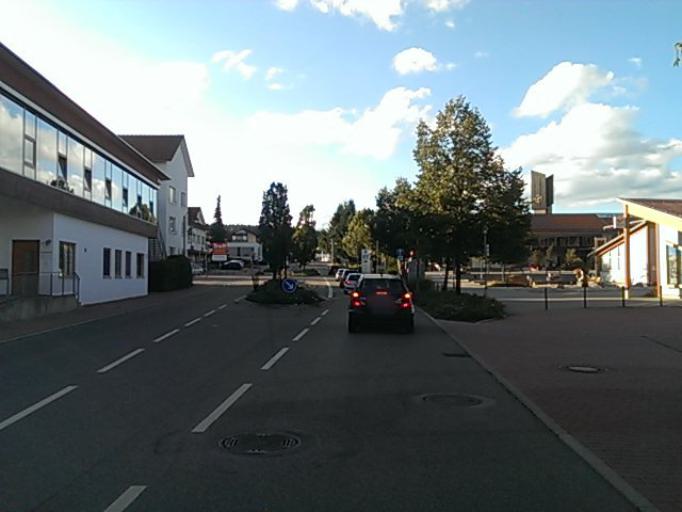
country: DE
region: Baden-Wuerttemberg
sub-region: Karlsruhe Region
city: Lossburg
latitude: 48.4136
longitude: 8.4503
